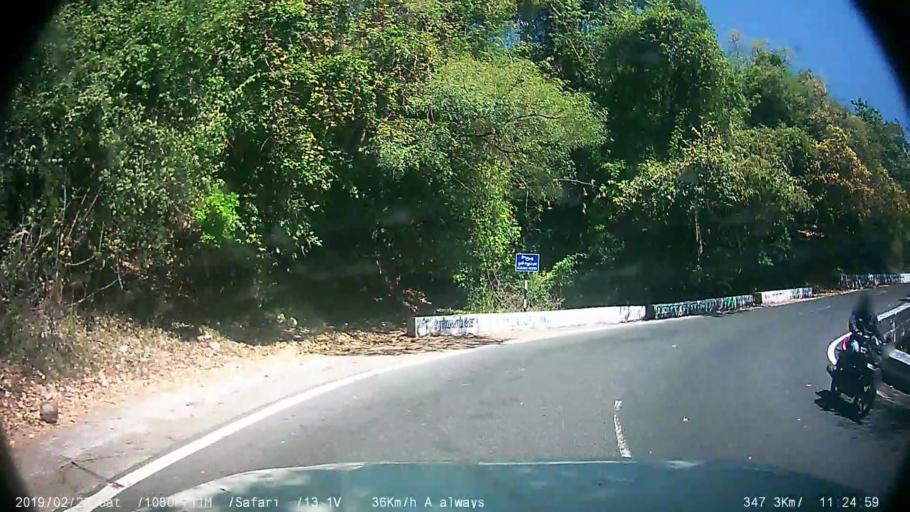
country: IN
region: Tamil Nadu
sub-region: Coimbatore
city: Mettupalayam
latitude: 11.3399
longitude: 76.8722
